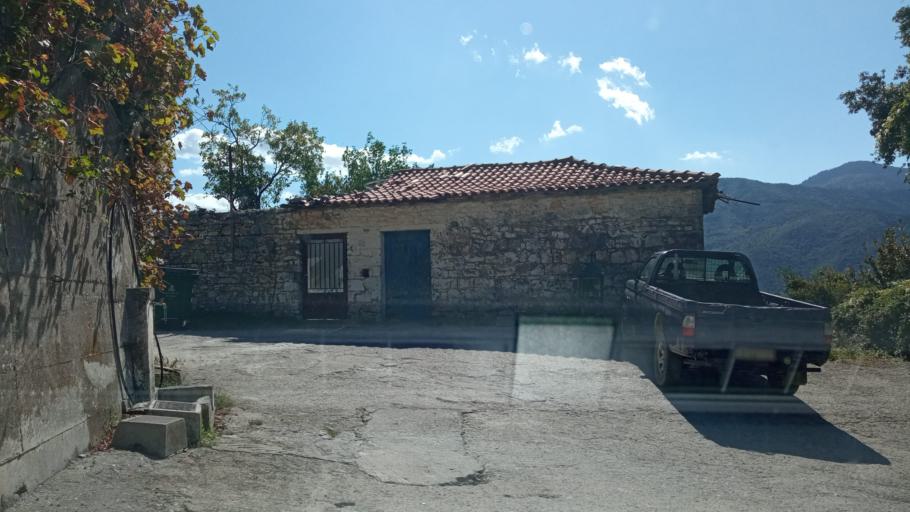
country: GR
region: Central Greece
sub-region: Nomos Evvoias
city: Kymi
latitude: 38.6511
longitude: 23.9059
